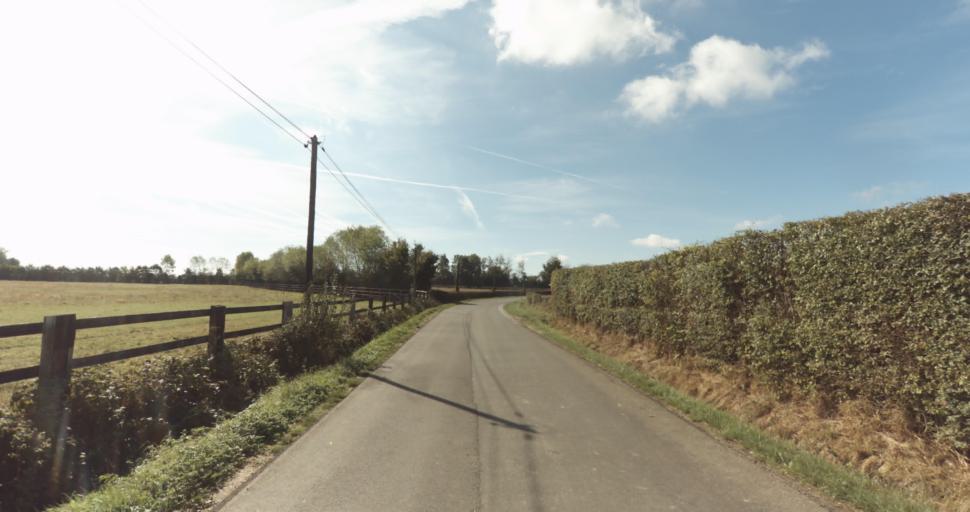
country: FR
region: Lower Normandy
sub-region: Departement du Calvados
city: La Vespiere
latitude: 48.9308
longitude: 0.3436
